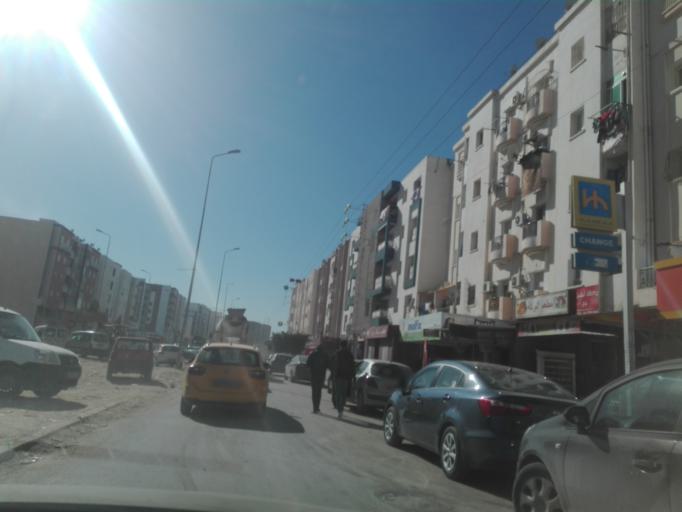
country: TN
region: Bin 'Arus
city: Ben Arous
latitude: 36.7156
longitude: 10.2159
